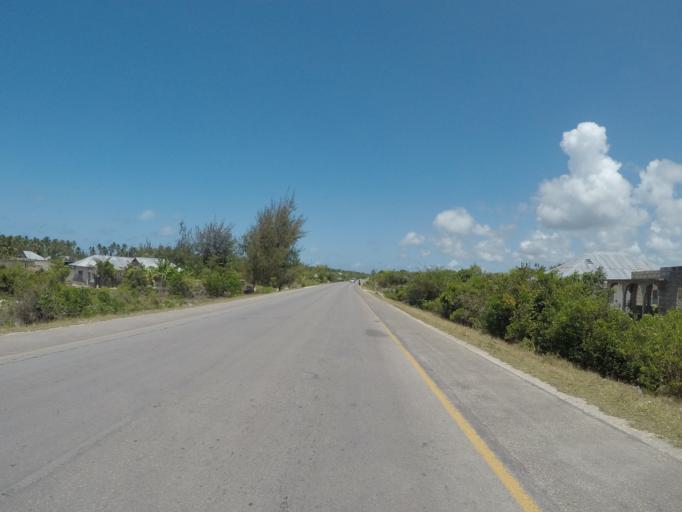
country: TZ
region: Zanzibar Central/South
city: Nganane
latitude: -6.3060
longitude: 39.5397
